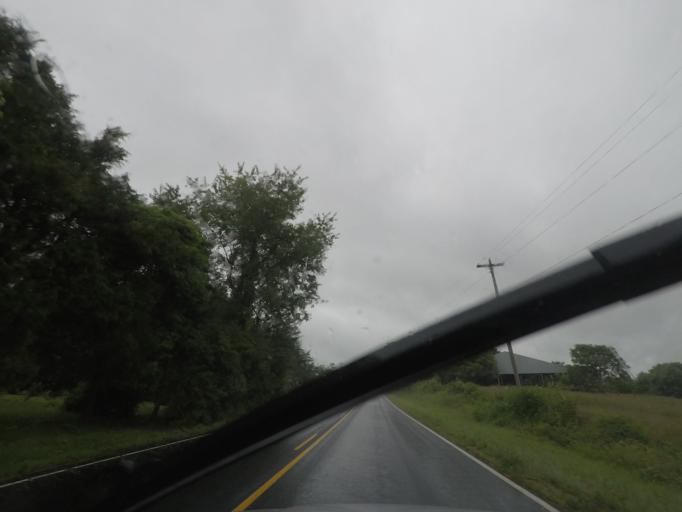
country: US
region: Virginia
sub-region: Culpeper County
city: Merrimac
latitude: 38.3773
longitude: -78.0968
